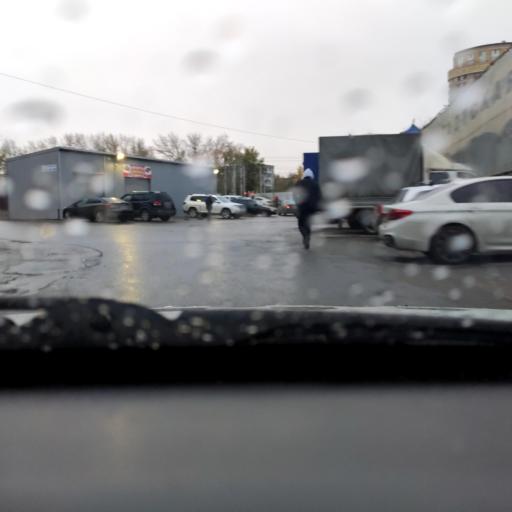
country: RU
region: Perm
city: Perm
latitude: 57.9956
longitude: 56.2030
